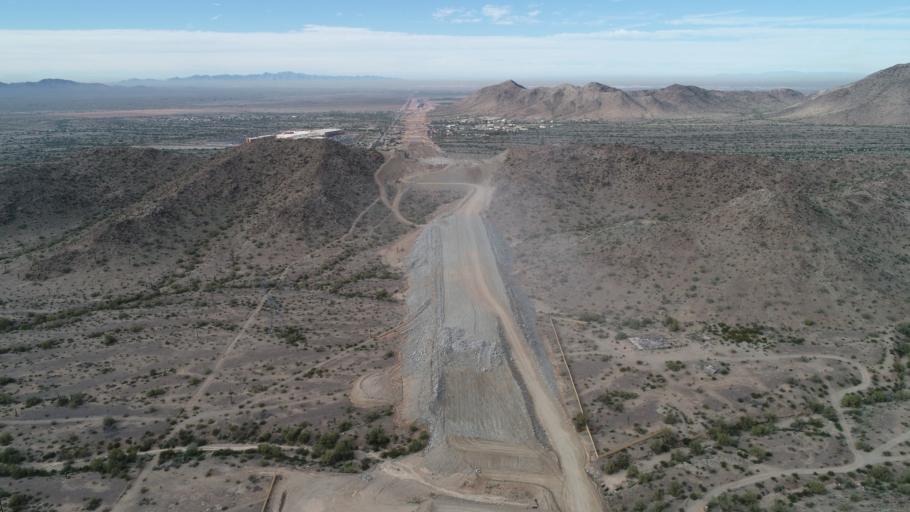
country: US
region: Arizona
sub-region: Maricopa County
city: Laveen
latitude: 33.2991
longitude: -112.1404
